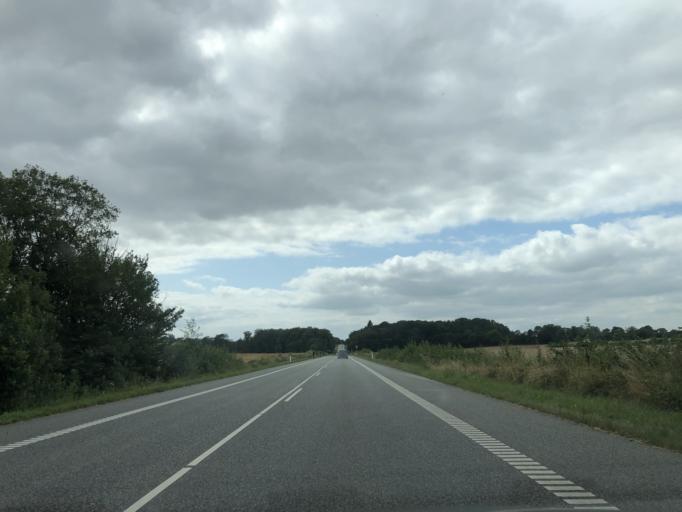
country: DK
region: South Denmark
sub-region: Sonderborg Kommune
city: Guderup
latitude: 54.9854
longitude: 9.9733
